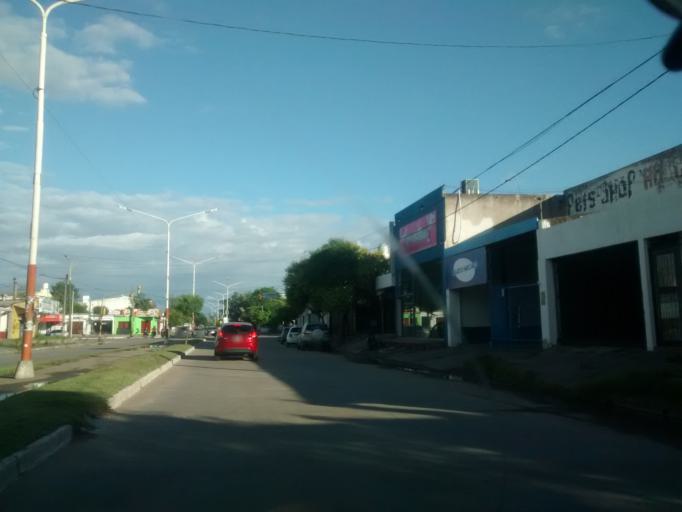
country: AR
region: Chaco
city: Resistencia
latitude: -27.4634
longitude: -59.0014
